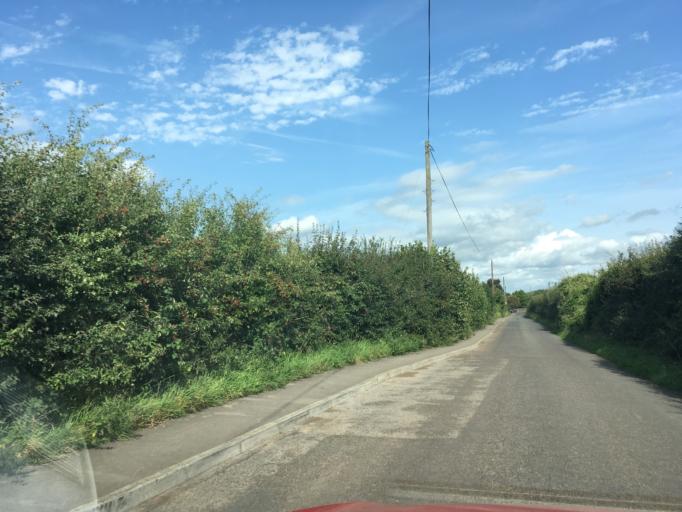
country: GB
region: England
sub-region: South Gloucestershire
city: Falfield
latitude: 51.6122
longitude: -2.4433
